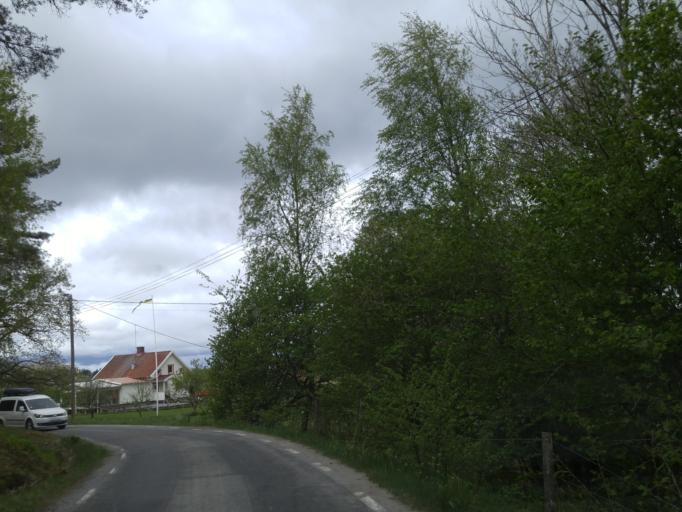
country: SE
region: Vaestra Goetaland
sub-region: Stenungsunds Kommun
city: Stora Hoga
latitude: 57.9969
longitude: 11.8582
